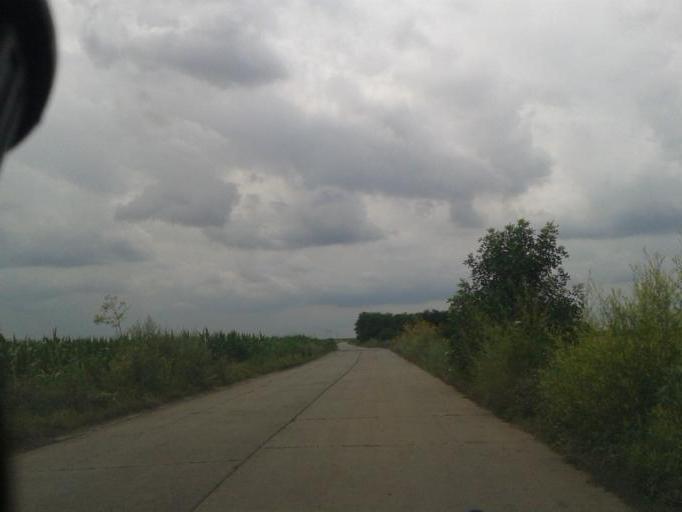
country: RO
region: Calarasi
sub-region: Comuna Fundulea
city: Fundulea
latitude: 44.4880
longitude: 26.5222
